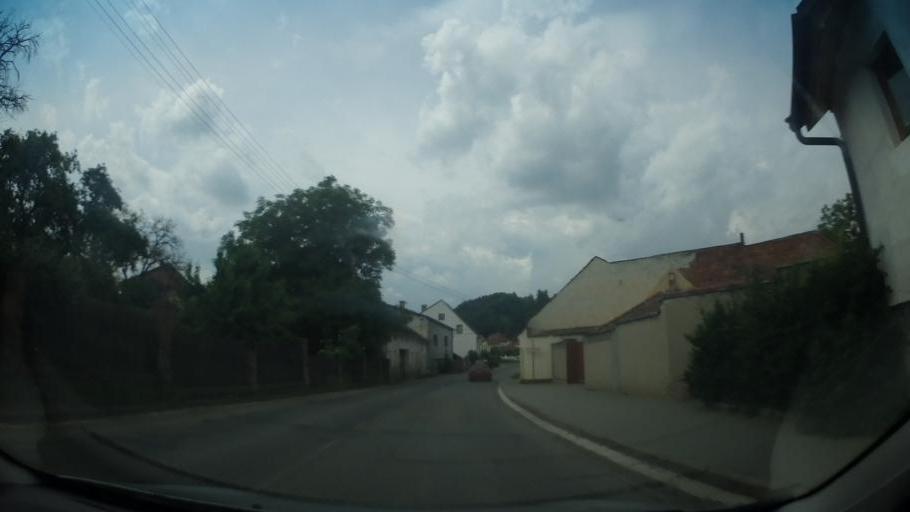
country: CZ
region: South Moravian
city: Lysice
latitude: 49.4509
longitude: 16.5388
